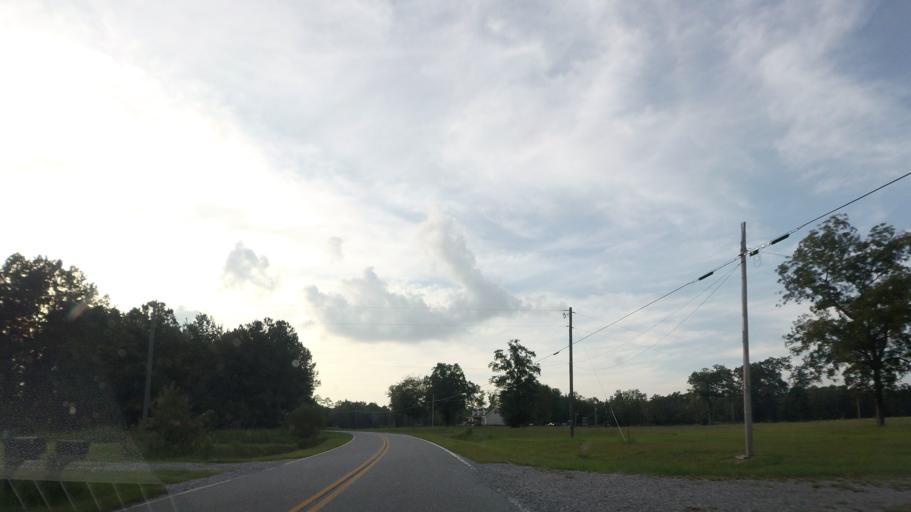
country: US
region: Georgia
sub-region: Wilkinson County
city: Gordon
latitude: 32.8626
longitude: -83.4606
